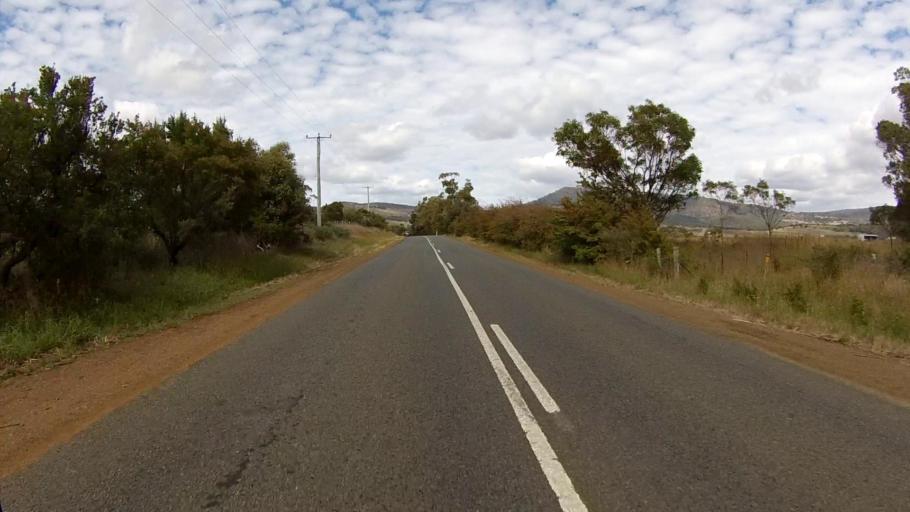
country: AU
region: Tasmania
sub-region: Clarence
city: Cambridge
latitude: -42.7469
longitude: 147.4151
